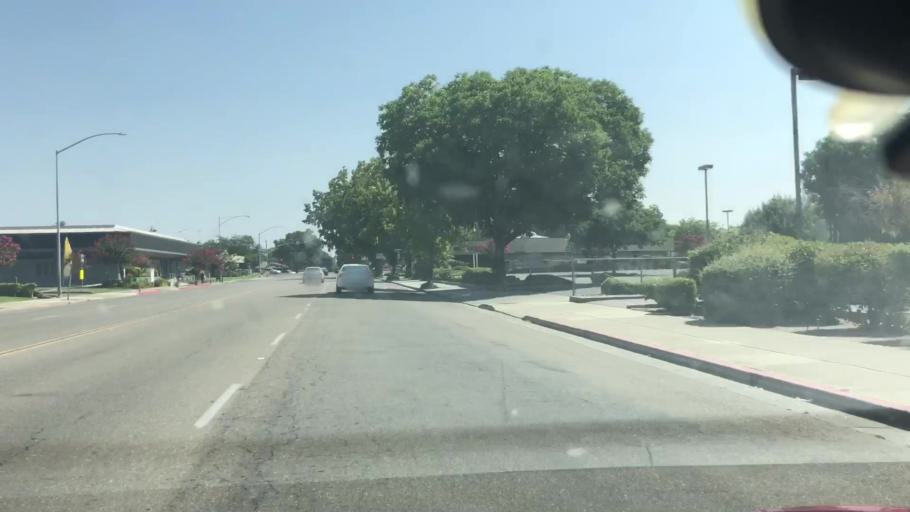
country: US
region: California
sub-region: San Joaquin County
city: Lincoln Village
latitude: 37.9982
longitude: -121.3080
